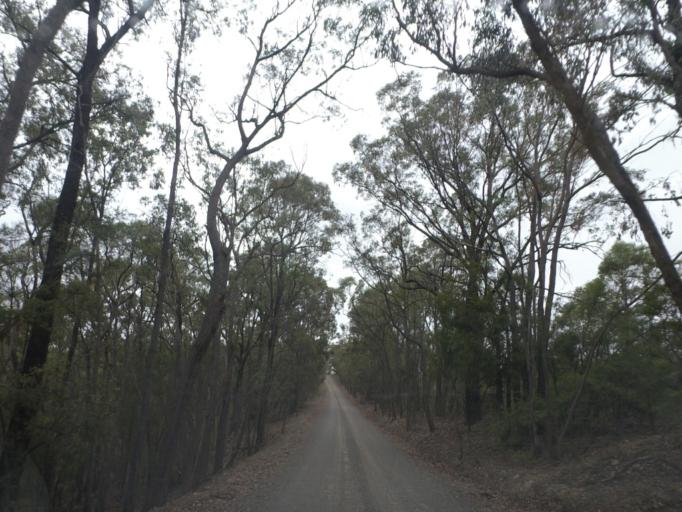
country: AU
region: Victoria
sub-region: Yarra Ranges
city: Chirnside Park
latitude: -37.6918
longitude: 145.3058
